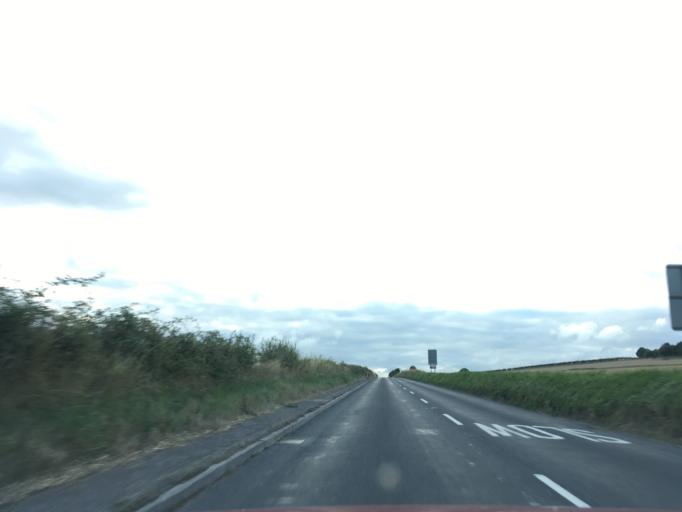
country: GB
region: England
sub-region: Wiltshire
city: Devizes
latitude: 51.3343
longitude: -1.9496
